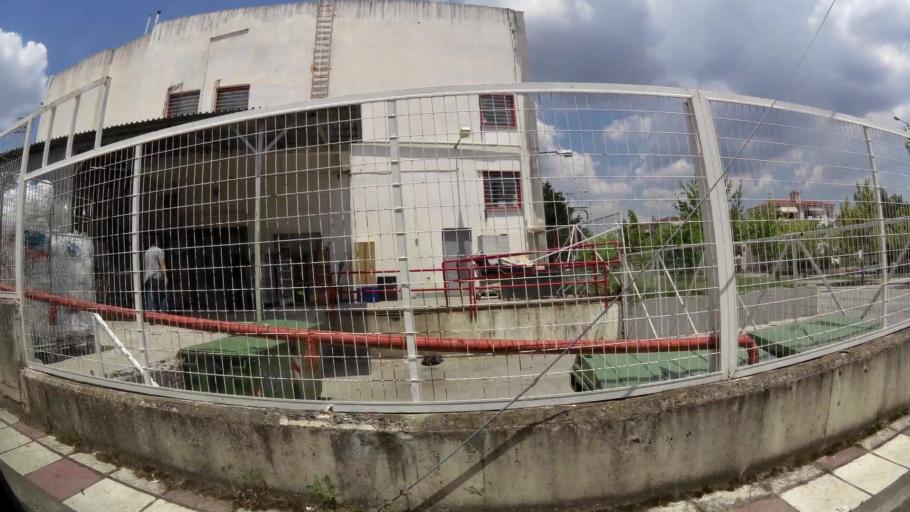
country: GR
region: West Macedonia
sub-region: Nomos Kozanis
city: Kozani
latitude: 40.2921
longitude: 21.7832
